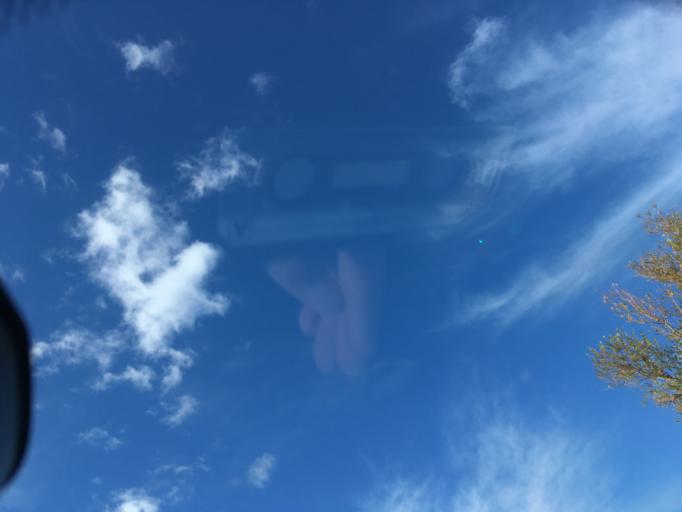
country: FR
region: Languedoc-Roussillon
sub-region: Departement de l'Herault
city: Lattes
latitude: 43.5821
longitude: 3.8906
